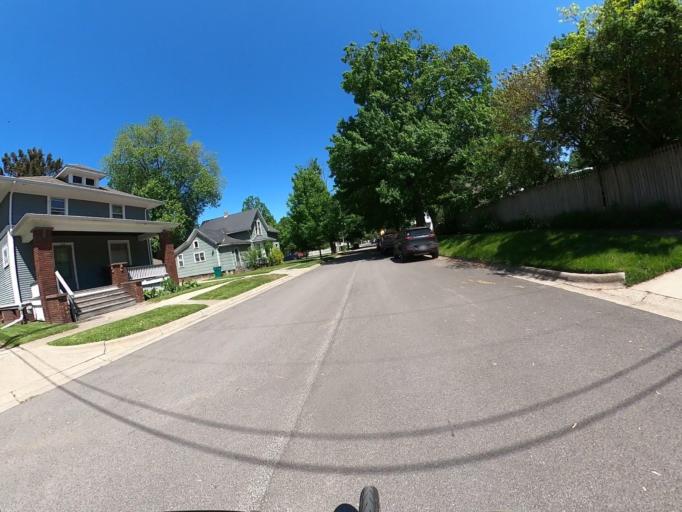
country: US
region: Indiana
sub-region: LaPorte County
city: LaPorte
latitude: 41.6047
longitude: -86.7262
